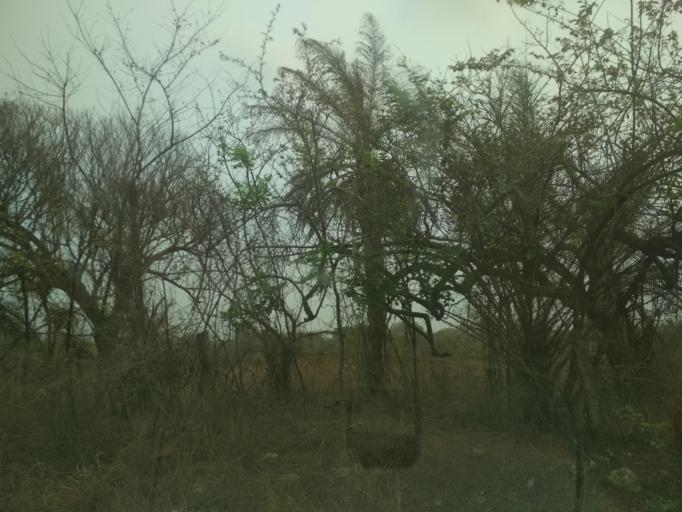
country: MX
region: Veracruz
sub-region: Veracruz
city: Delfino Victoria (Santa Fe)
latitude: 19.2100
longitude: -96.2607
